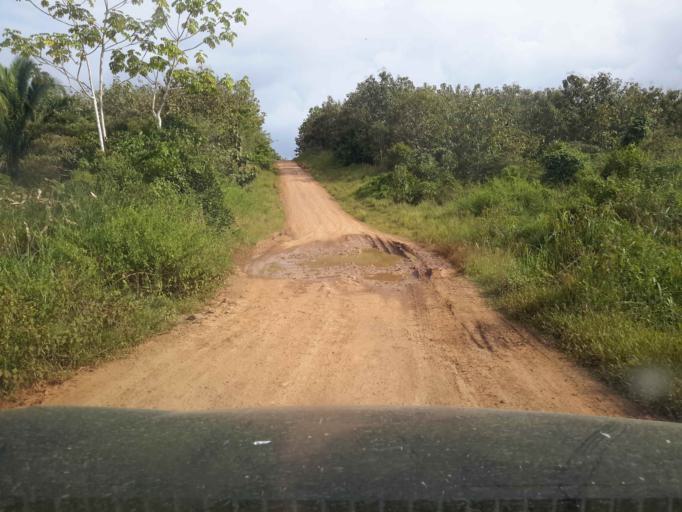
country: CR
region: Alajuela
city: Los Chiles
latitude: 11.0882
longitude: -84.5437
